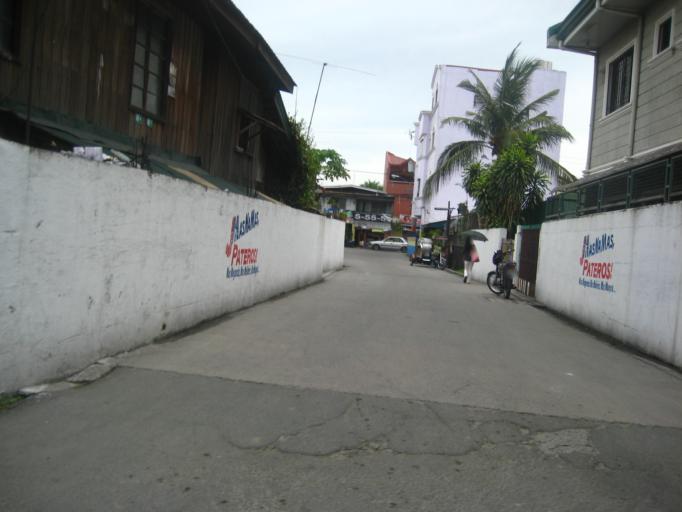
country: PH
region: Calabarzon
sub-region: Province of Rizal
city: Pateros
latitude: 14.5411
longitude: 121.0688
